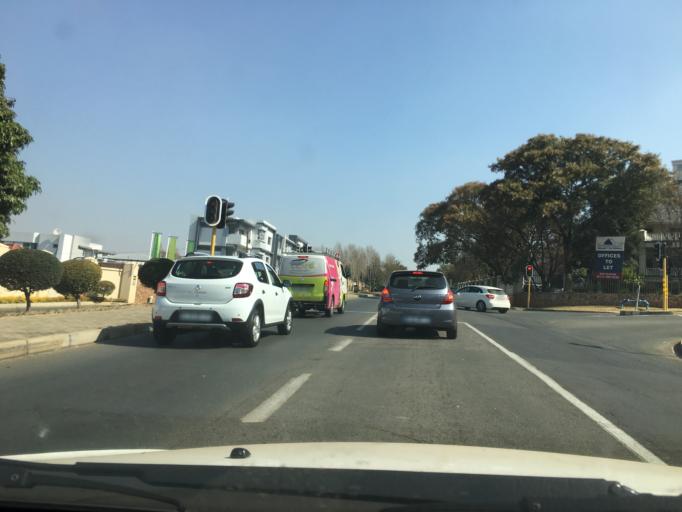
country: ZA
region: Gauteng
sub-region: City of Johannesburg Metropolitan Municipality
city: Johannesburg
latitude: -26.0749
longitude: 28.0314
